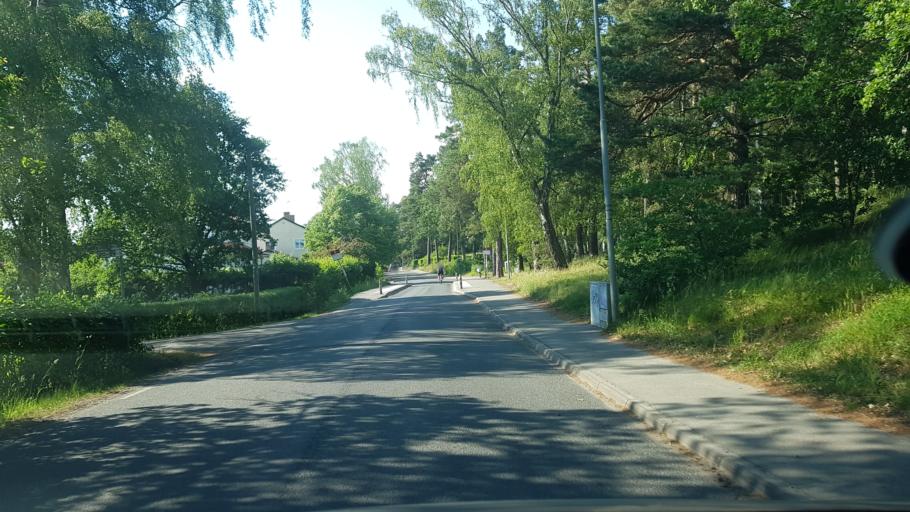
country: SE
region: Stockholm
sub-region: Sollentuna Kommun
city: Sollentuna
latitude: 59.4211
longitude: 17.9680
